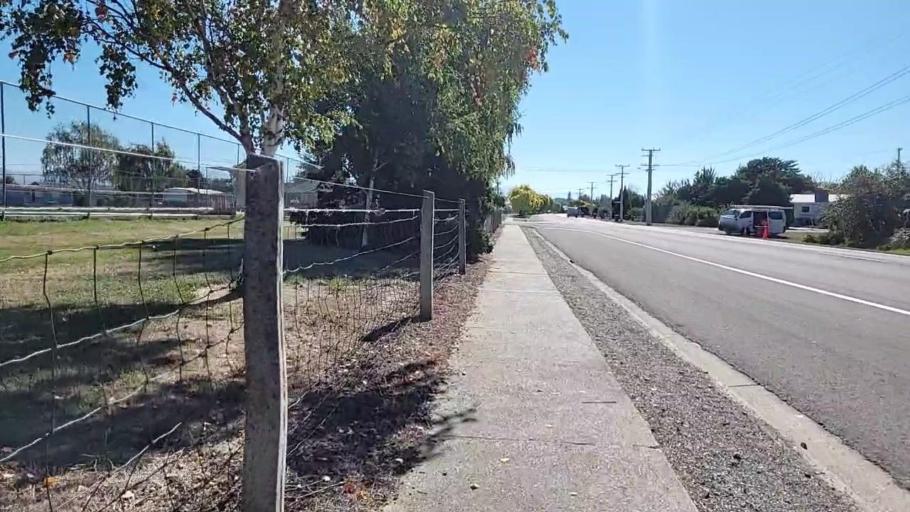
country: NZ
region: Otago
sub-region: Queenstown-Lakes District
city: Wanaka
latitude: -45.1002
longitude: 169.5968
